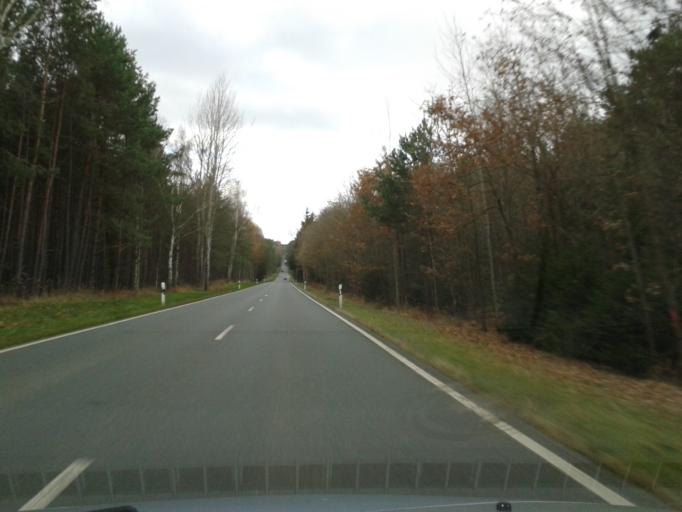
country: DE
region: Thuringia
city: Hermsdorf
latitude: 50.9174
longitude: 11.8371
